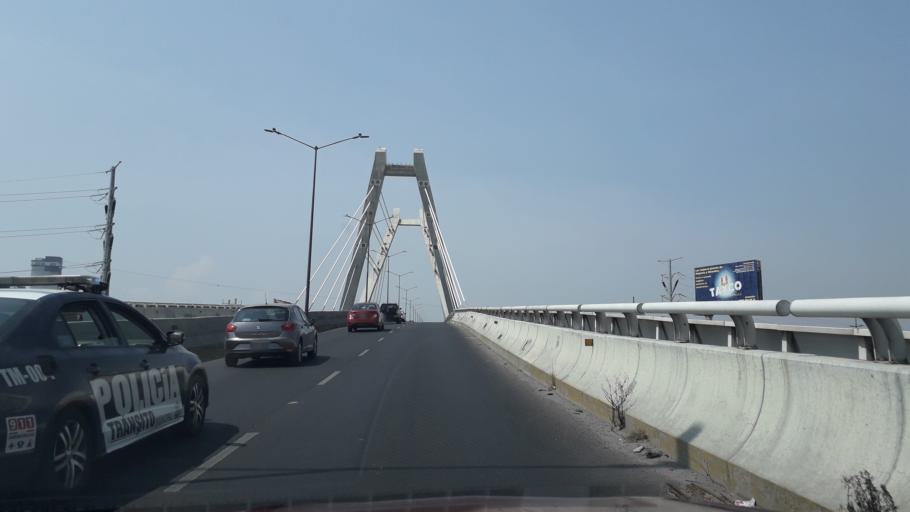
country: MX
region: Puebla
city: Puebla
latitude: 19.0653
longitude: -98.1791
